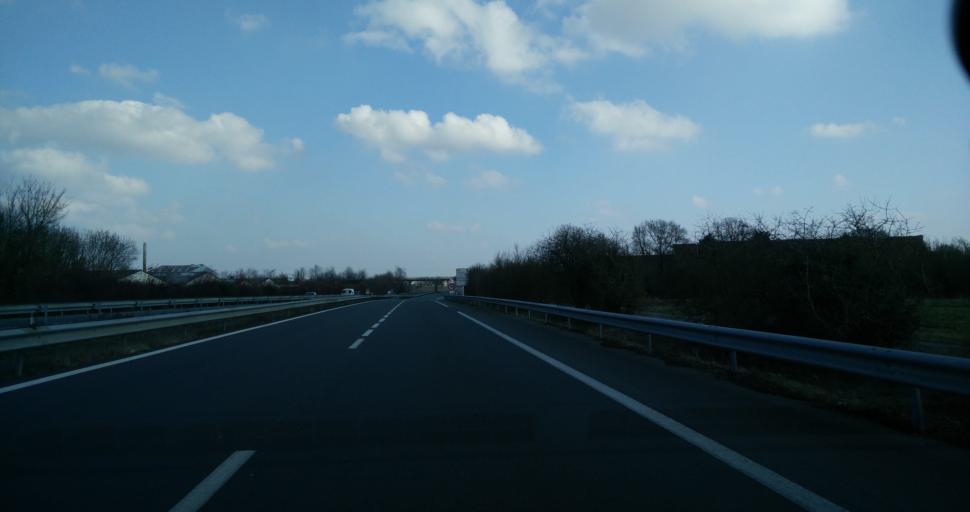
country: FR
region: Poitou-Charentes
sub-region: Departement de la Charente-Maritime
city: Saint-Jean-de-Liversay
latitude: 46.2266
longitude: -0.8837
